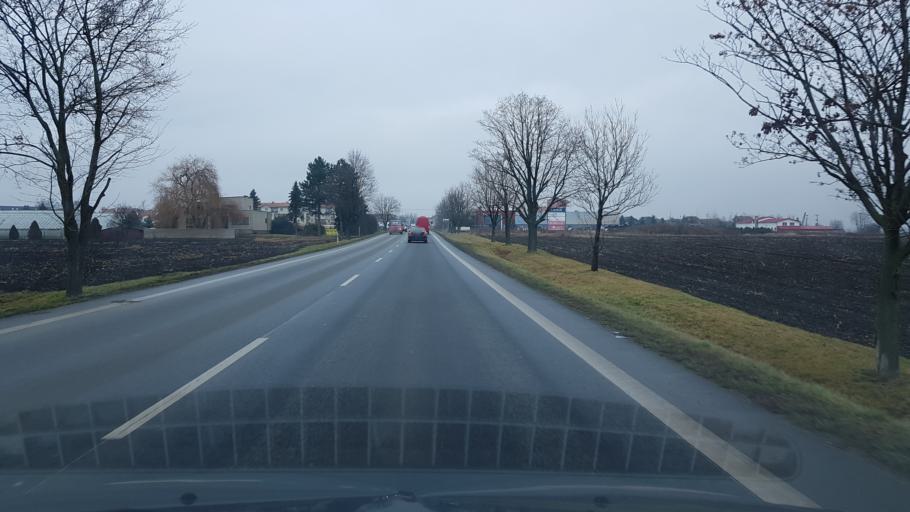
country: PL
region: Lower Silesian Voivodeship
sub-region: Powiat wroclawski
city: Bielany Wroclawskie
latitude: 51.0238
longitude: 16.9660
